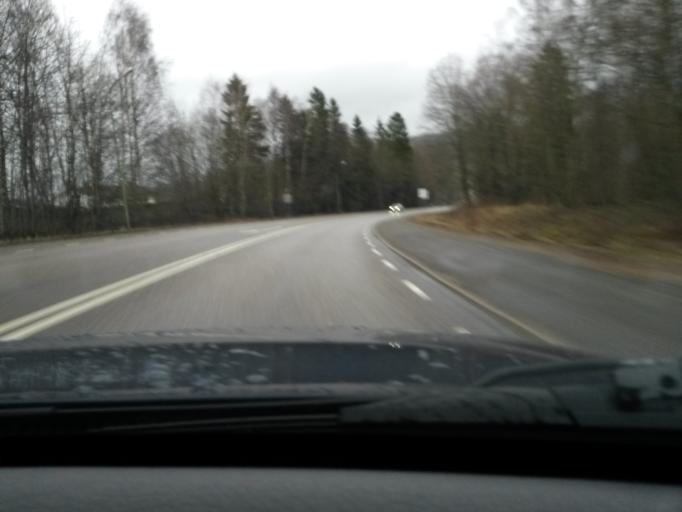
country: SE
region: Vaestra Goetaland
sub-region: Boras Kommun
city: Boras
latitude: 57.7591
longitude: 12.9542
